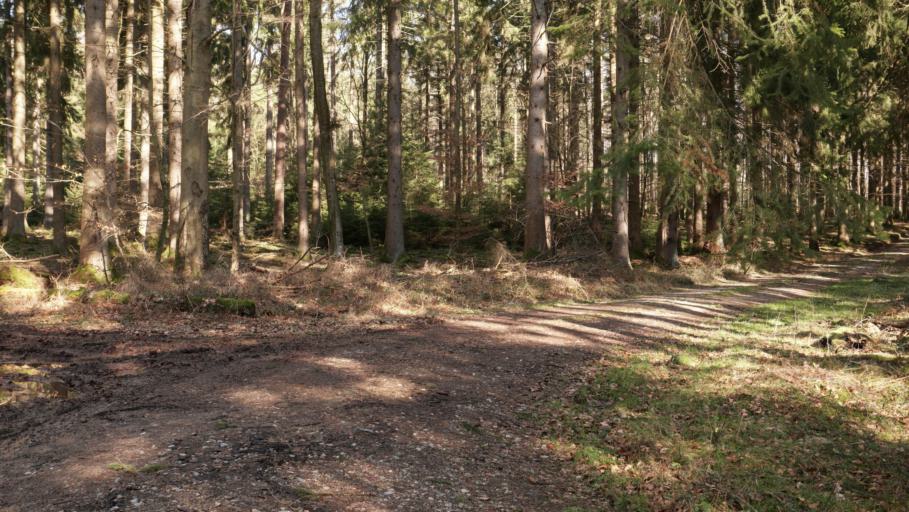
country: DE
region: Baden-Wuerttemberg
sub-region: Karlsruhe Region
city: Fahrenbach
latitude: 49.4513
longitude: 9.1165
